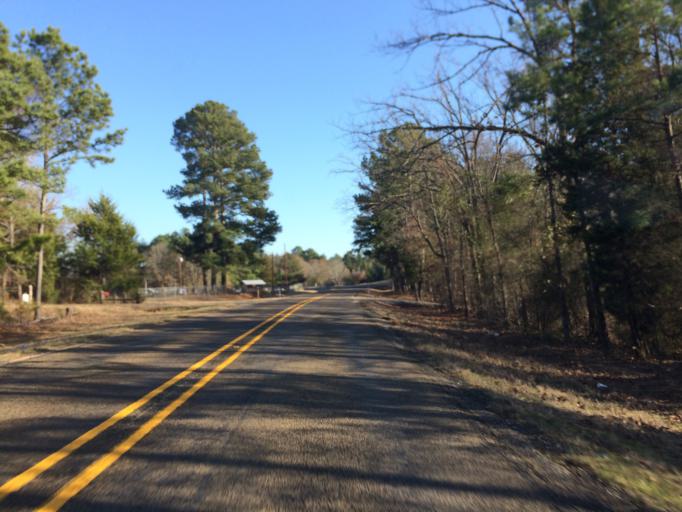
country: US
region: Texas
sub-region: Wood County
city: Mineola
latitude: 32.6876
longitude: -95.3409
